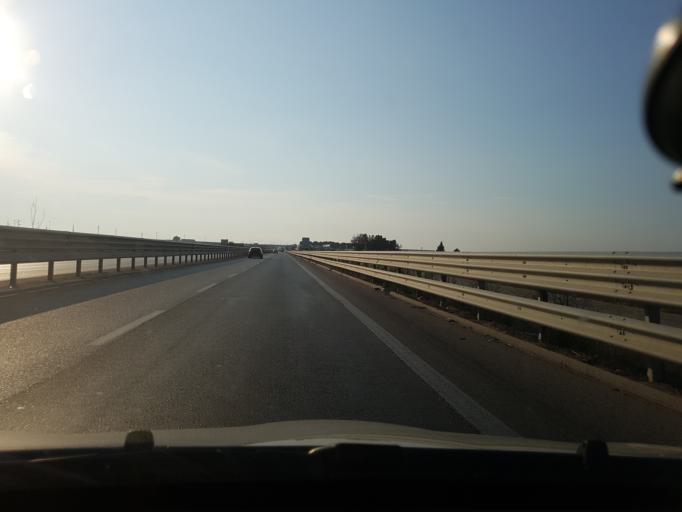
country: IT
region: Apulia
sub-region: Provincia di Foggia
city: Stornara
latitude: 41.2926
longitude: 15.8324
